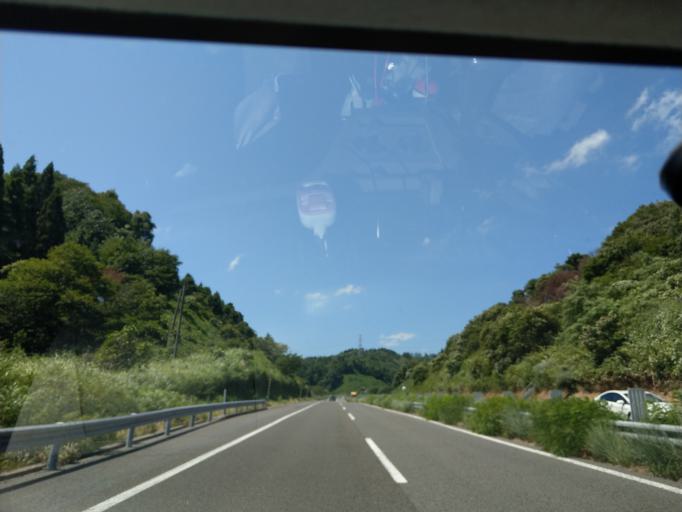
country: JP
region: Akita
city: Omagari
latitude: 39.5697
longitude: 140.3044
